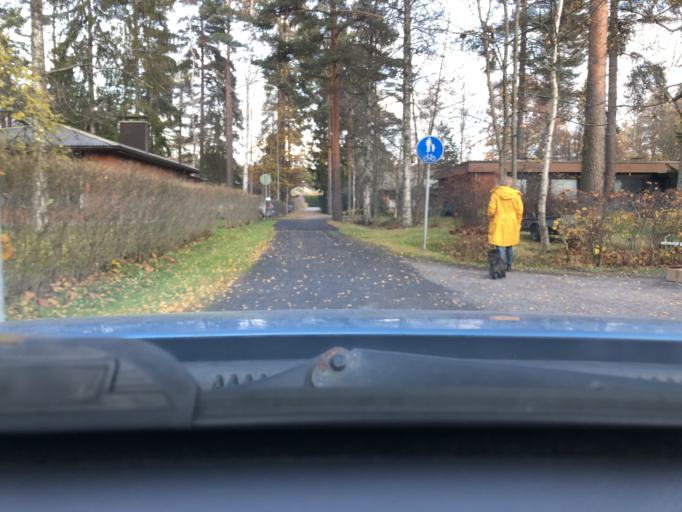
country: FI
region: Pirkanmaa
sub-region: Tampere
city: Kangasala
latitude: 61.4683
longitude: 24.0276
